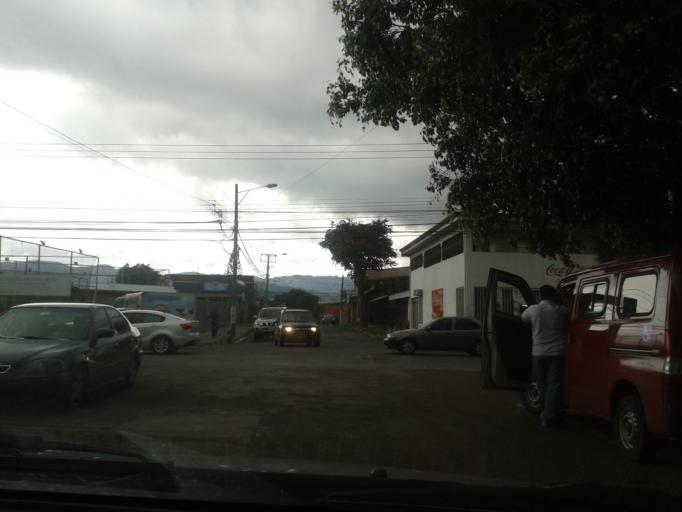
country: CR
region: San Jose
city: San Miguel
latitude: 9.8976
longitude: -84.0615
